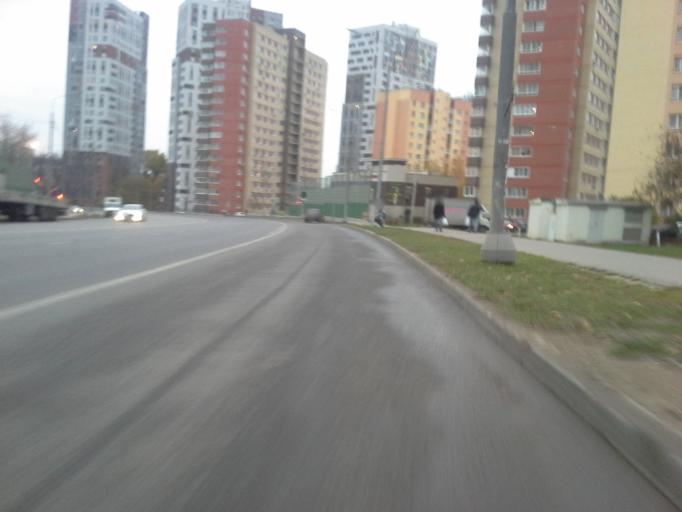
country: RU
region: Moskovskaya
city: Kommunarka
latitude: 55.5691
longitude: 37.4769
